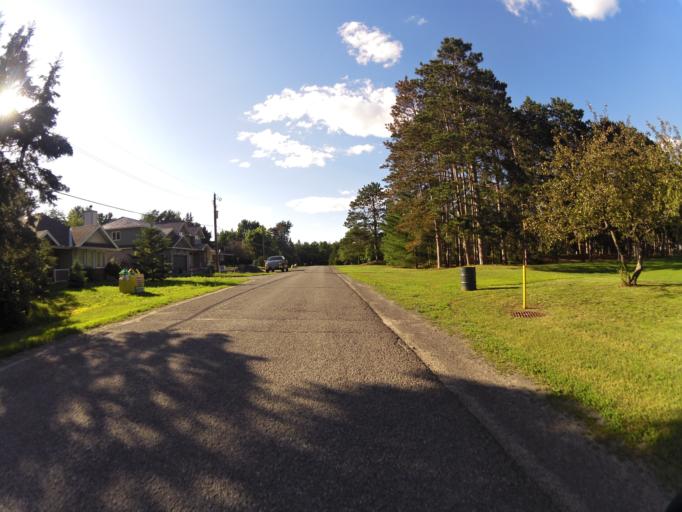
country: CA
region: Ontario
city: Bells Corners
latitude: 45.3217
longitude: -75.7405
